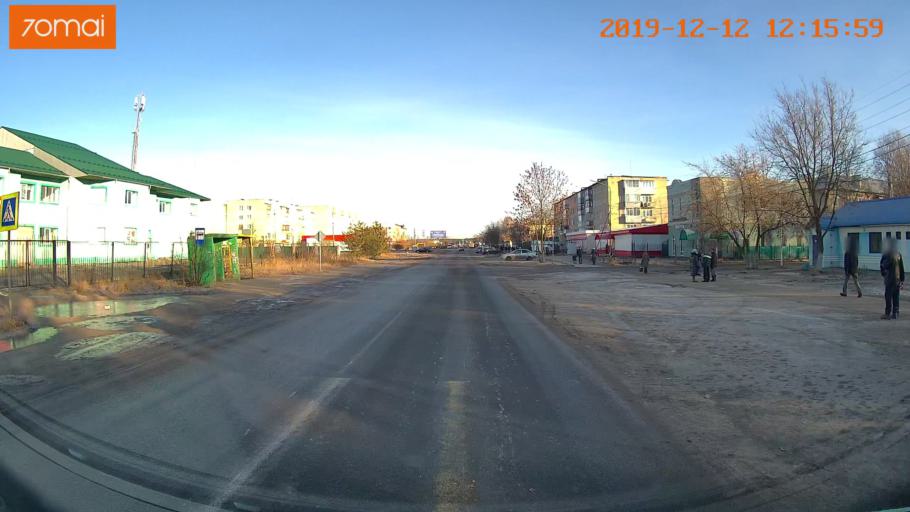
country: RU
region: Ivanovo
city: Kokhma
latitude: 56.9388
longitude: 41.1043
